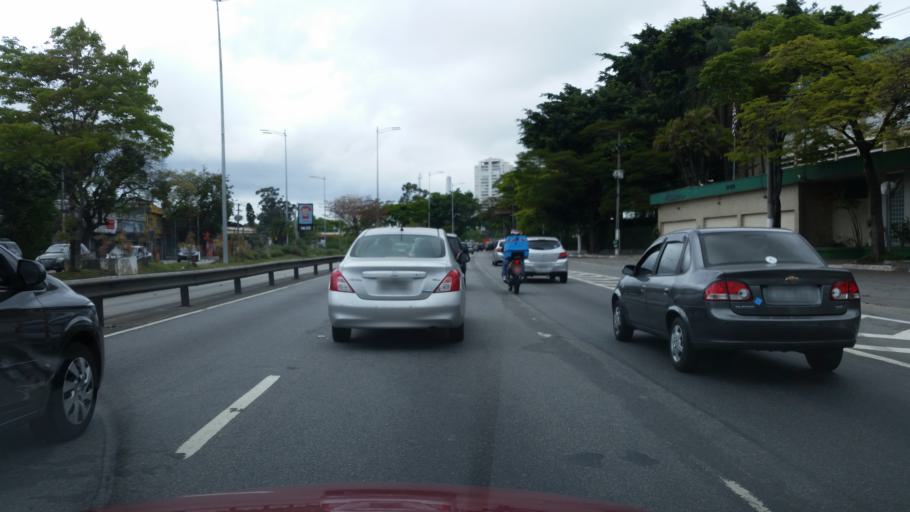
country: BR
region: Sao Paulo
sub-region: Diadema
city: Diadema
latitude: -23.6655
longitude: -46.7085
